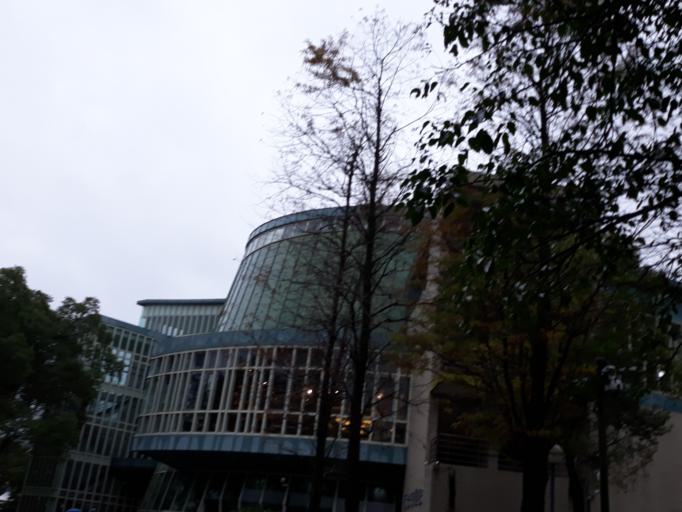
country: TW
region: Taipei
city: Taipei
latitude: 24.9969
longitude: 121.5832
